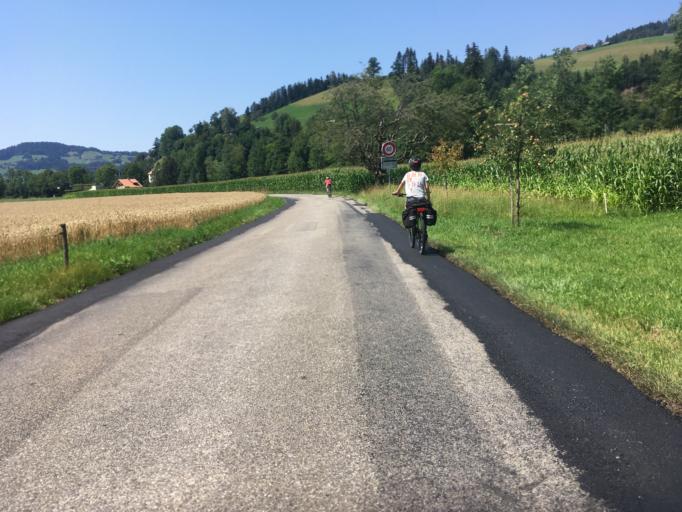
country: CH
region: Bern
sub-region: Emmental District
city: Langnau
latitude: 46.9425
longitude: 7.7724
